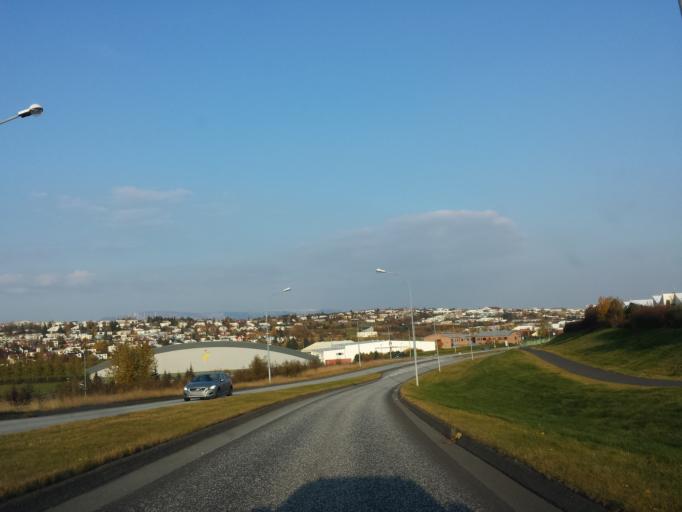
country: IS
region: Capital Region
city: Kopavogur
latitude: 64.1006
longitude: -21.9028
